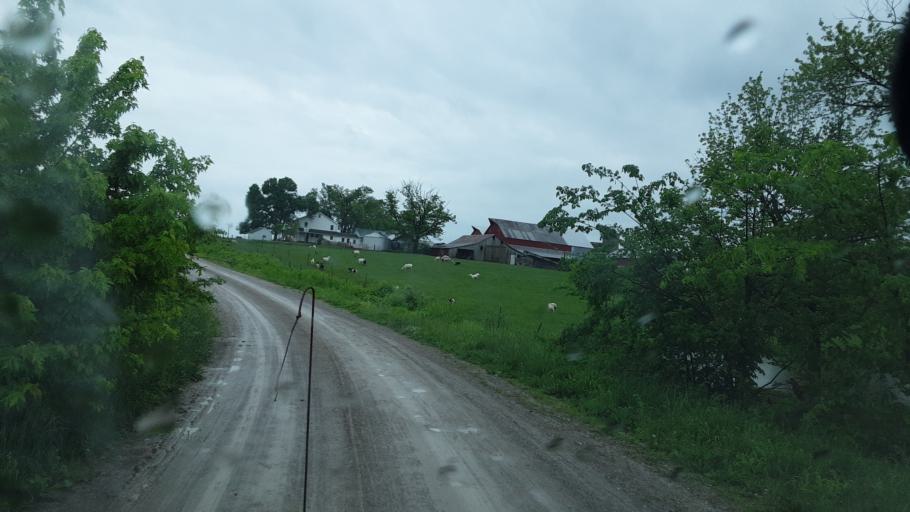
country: US
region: Missouri
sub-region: Randolph County
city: Moberly
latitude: 39.3094
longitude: -92.3052
